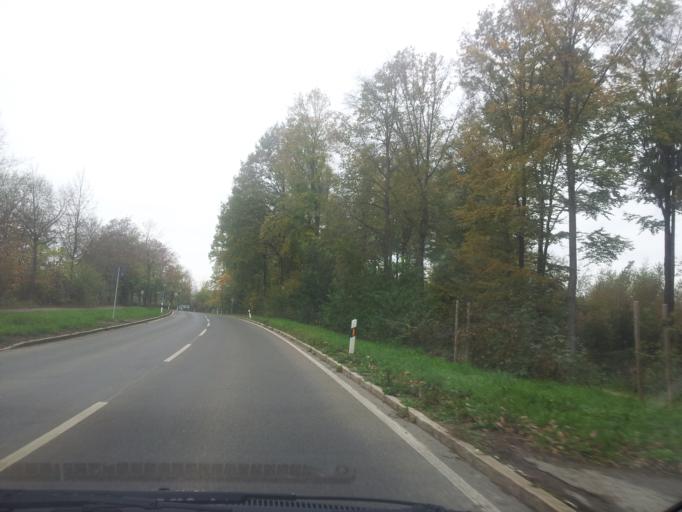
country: DE
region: Baden-Wuerttemberg
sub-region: Regierungsbezirk Stuttgart
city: Esslingen
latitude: 48.7543
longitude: 9.3459
